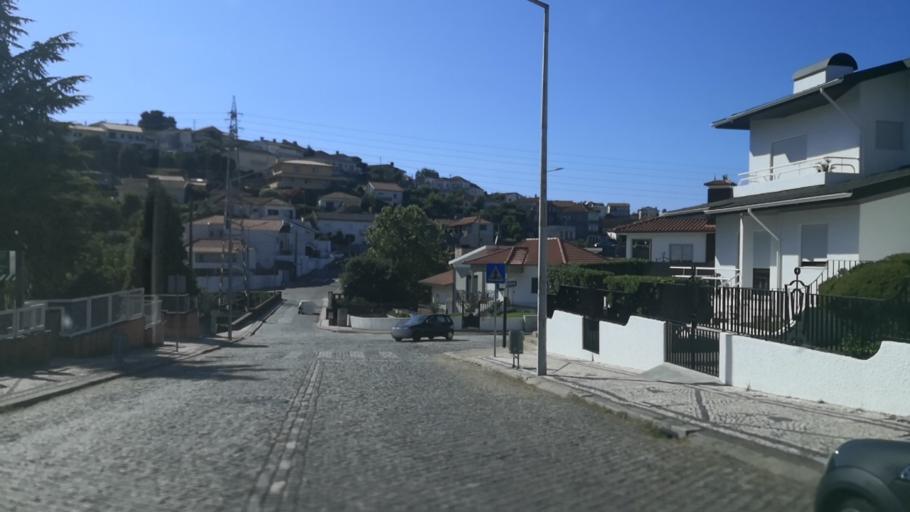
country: PT
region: Porto
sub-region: Santo Tirso
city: Santo Tirso
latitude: 41.3439
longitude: -8.4840
